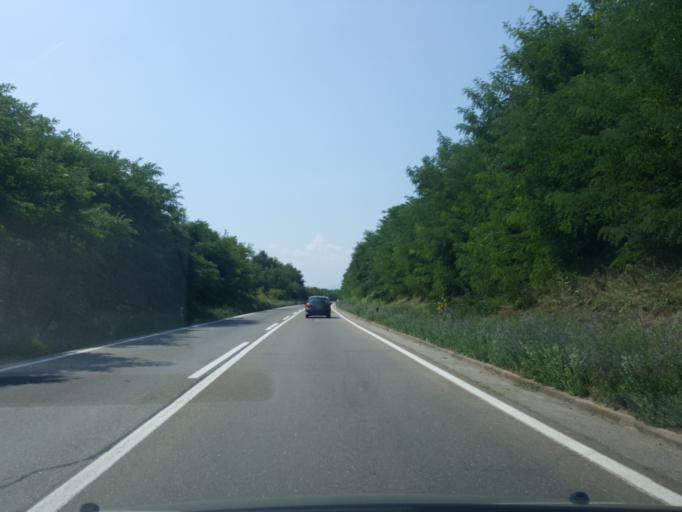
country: RS
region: Central Serbia
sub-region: Belgrade
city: Sopot
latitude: 44.5274
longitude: 20.6555
